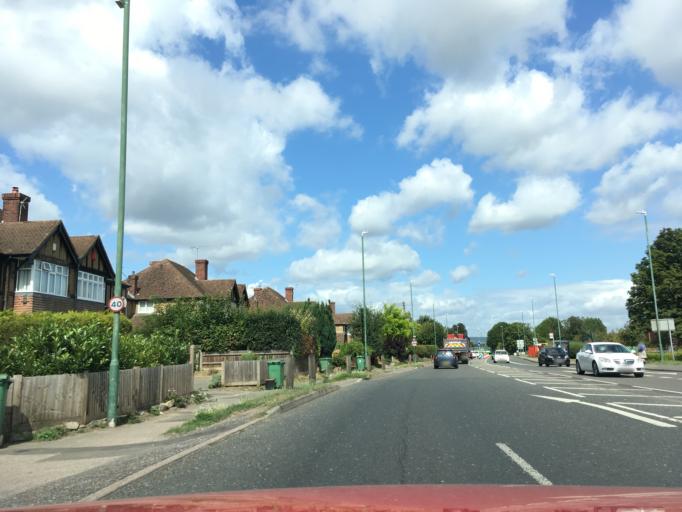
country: GB
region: England
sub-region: Kent
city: Aylesford
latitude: 51.2853
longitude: 0.4939
